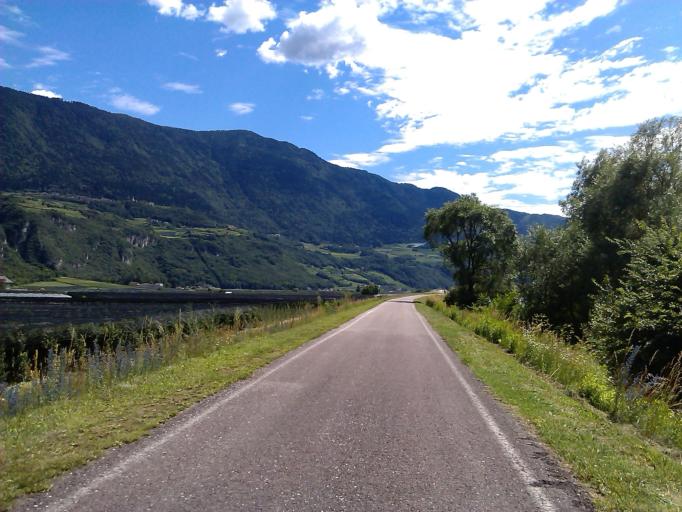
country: IT
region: Trentino-Alto Adige
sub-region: Bolzano
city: Laghetti
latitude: 46.2721
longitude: 11.2348
